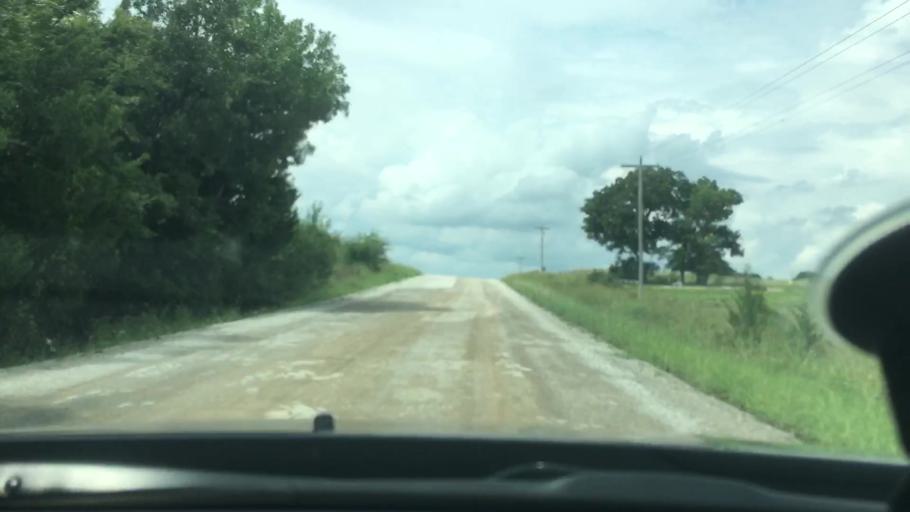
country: US
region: Oklahoma
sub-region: Carter County
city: Dickson
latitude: 34.2527
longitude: -96.9332
